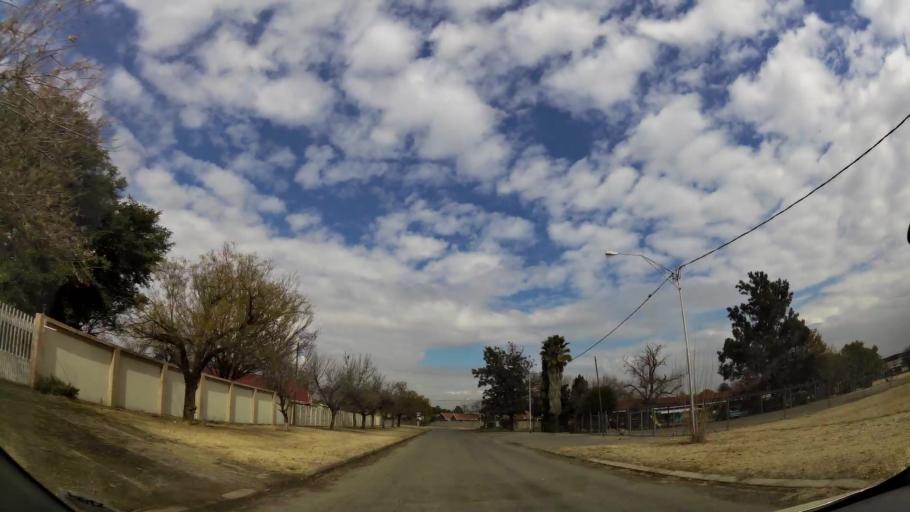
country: ZA
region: Gauteng
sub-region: Sedibeng District Municipality
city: Vereeniging
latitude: -26.6517
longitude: 27.9741
